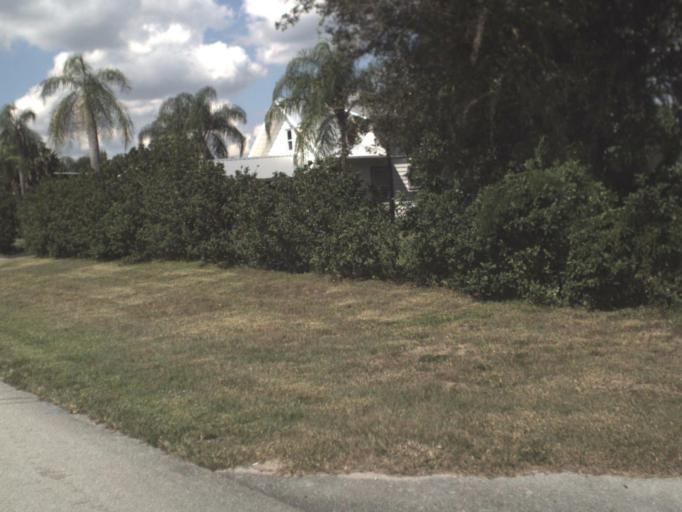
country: US
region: Florida
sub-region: Highlands County
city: Sebring
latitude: 27.4266
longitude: -81.4073
